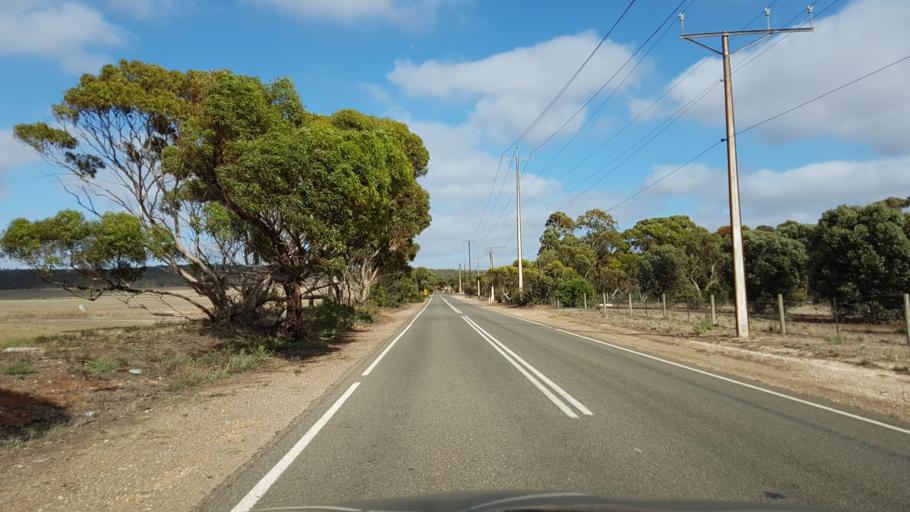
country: AU
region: South Australia
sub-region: Murray Bridge
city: Murray Bridge
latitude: -35.1178
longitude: 139.2400
